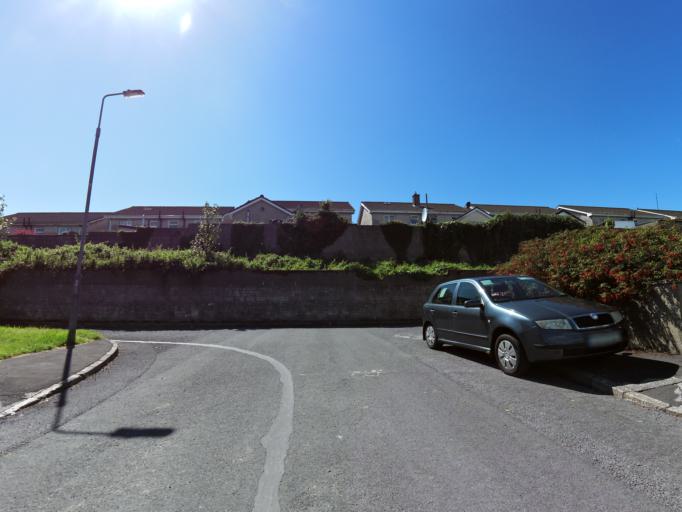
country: IE
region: Connaught
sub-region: County Galway
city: Gaillimh
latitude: 53.2833
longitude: -9.0756
